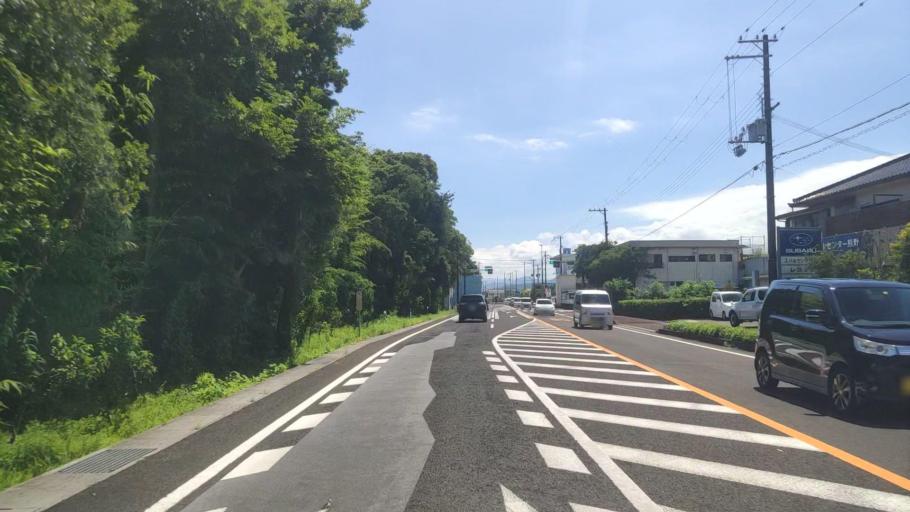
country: JP
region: Wakayama
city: Shingu
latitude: 33.8755
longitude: 136.0891
